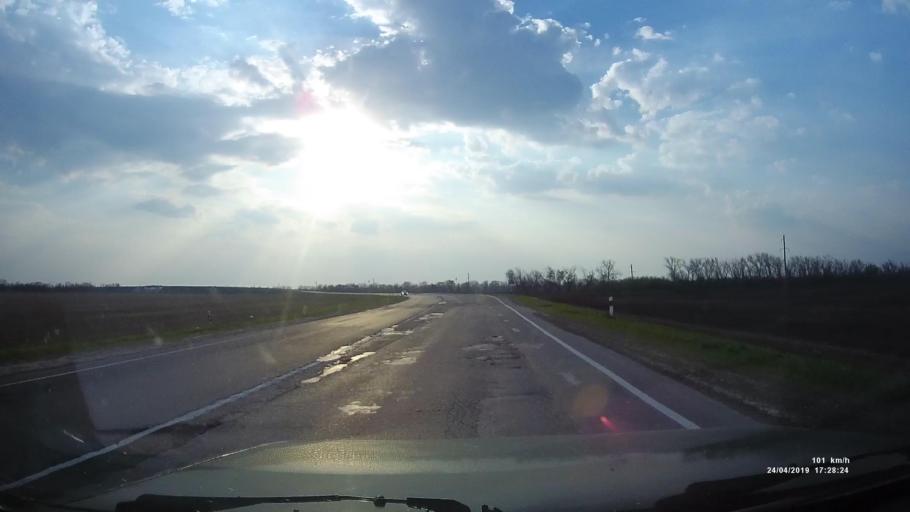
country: RU
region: Rostov
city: Tselina
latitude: 46.5322
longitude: 41.1783
